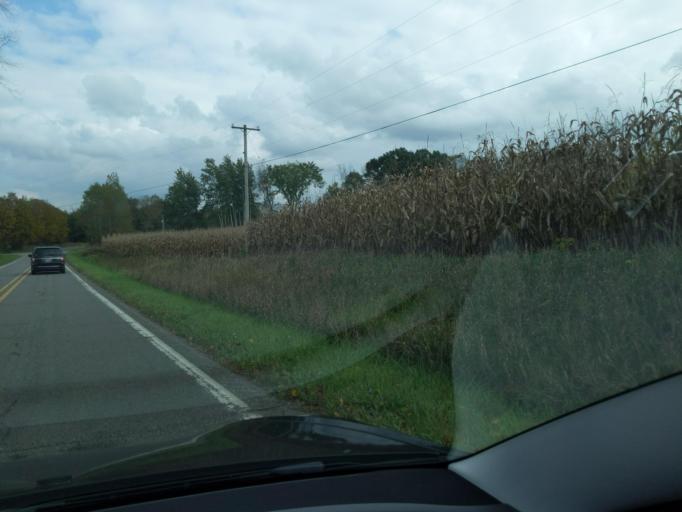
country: US
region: Michigan
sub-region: Ingham County
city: Leslie
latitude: 42.4118
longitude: -84.3859
